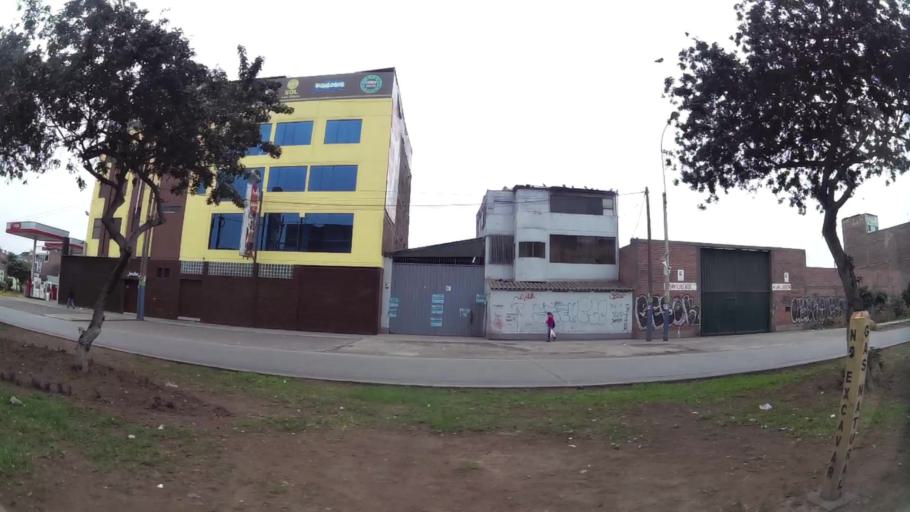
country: PE
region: Lima
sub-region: Lima
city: San Luis
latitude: -12.0746
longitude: -77.0015
